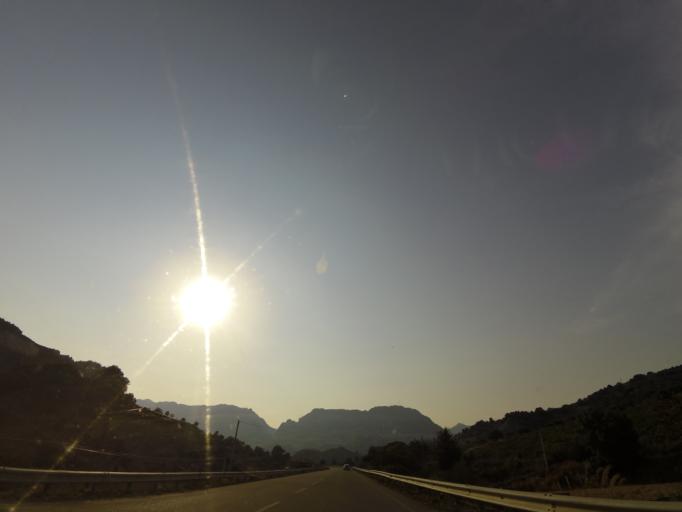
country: IT
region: Calabria
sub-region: Provincia di Reggio Calabria
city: Stilo
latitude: 38.4650
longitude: 16.4973
